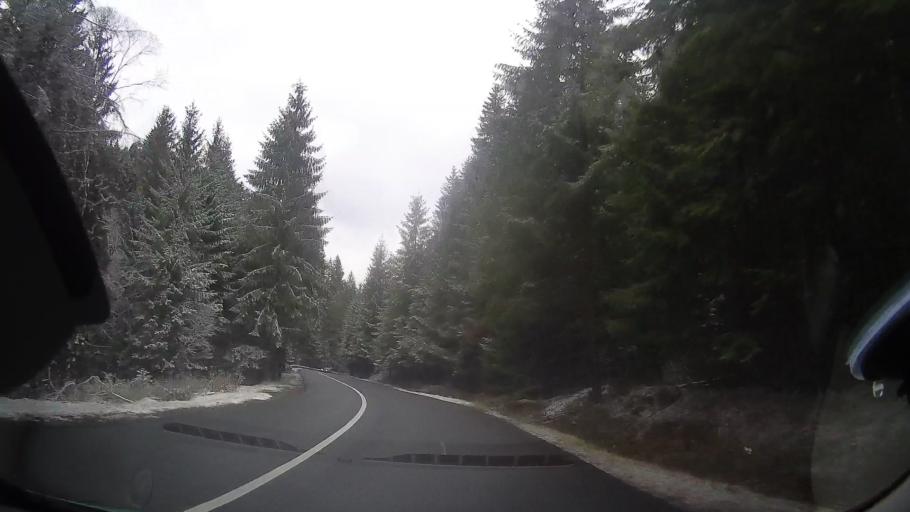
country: RO
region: Cluj
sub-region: Comuna Calatele
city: Calatele
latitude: 46.7359
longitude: 23.0391
